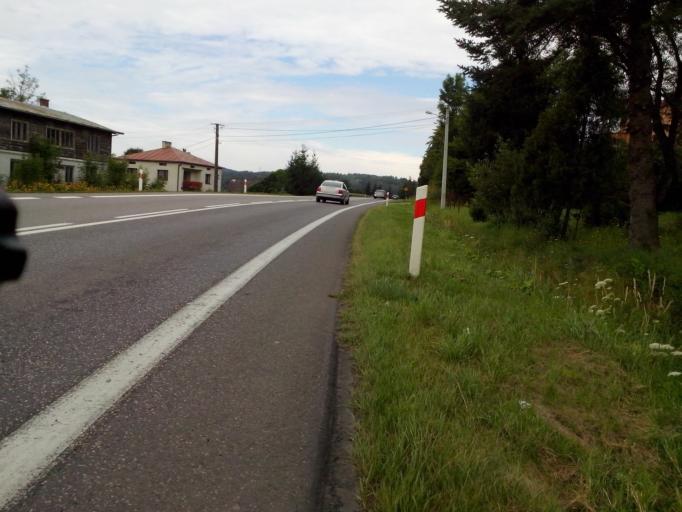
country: PL
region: Subcarpathian Voivodeship
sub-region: Powiat brzozowski
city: Blizne
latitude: 49.7665
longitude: 21.9572
